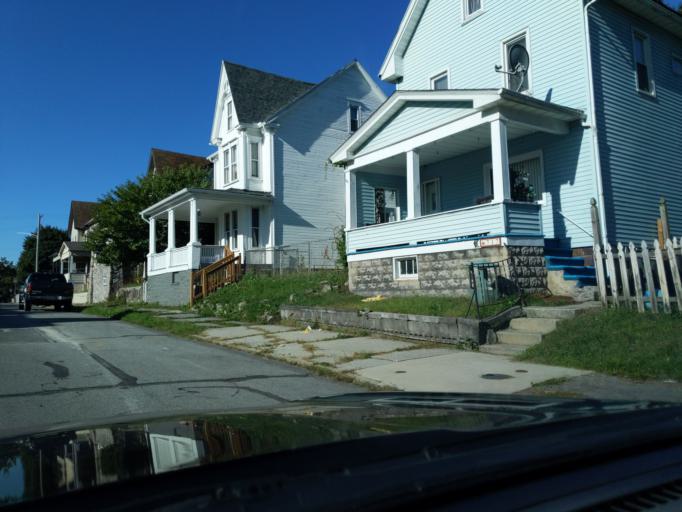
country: US
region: Pennsylvania
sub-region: Blair County
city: Greenwood
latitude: 40.5395
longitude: -78.3817
